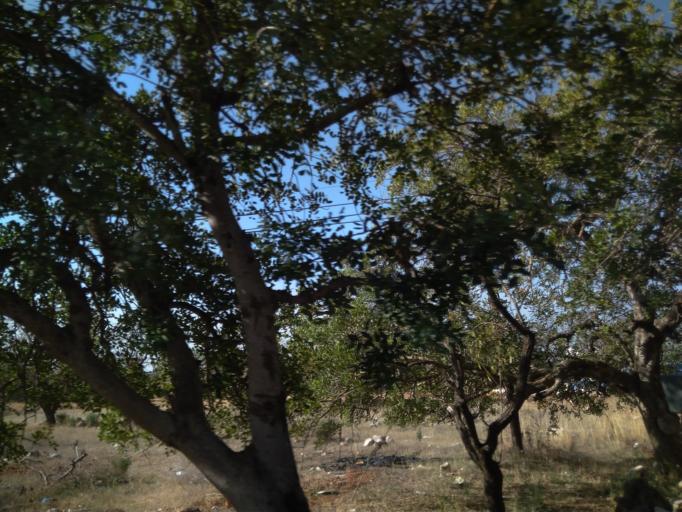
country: PT
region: Faro
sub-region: Faro
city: Santa Barbara de Nexe
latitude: 37.0918
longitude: -7.9619
